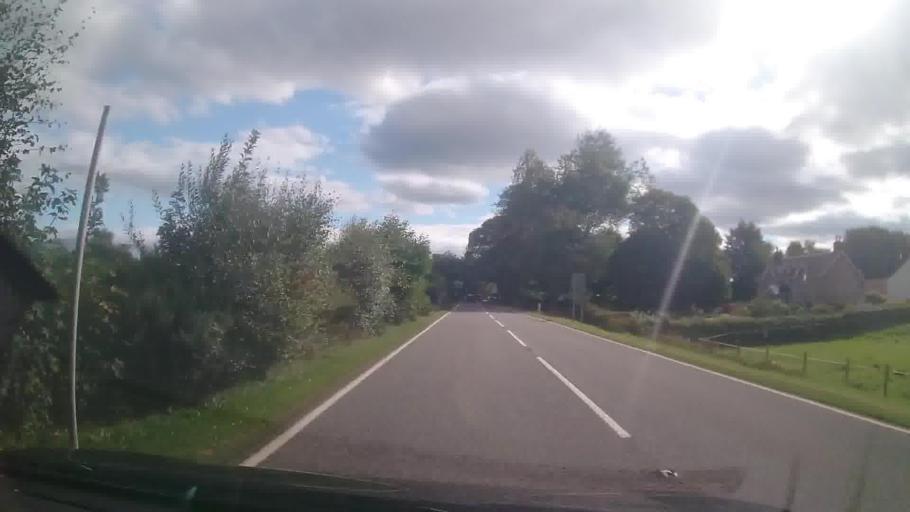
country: GB
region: Scotland
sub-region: Argyll and Bute
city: Oban
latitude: 56.4790
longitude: -5.3994
